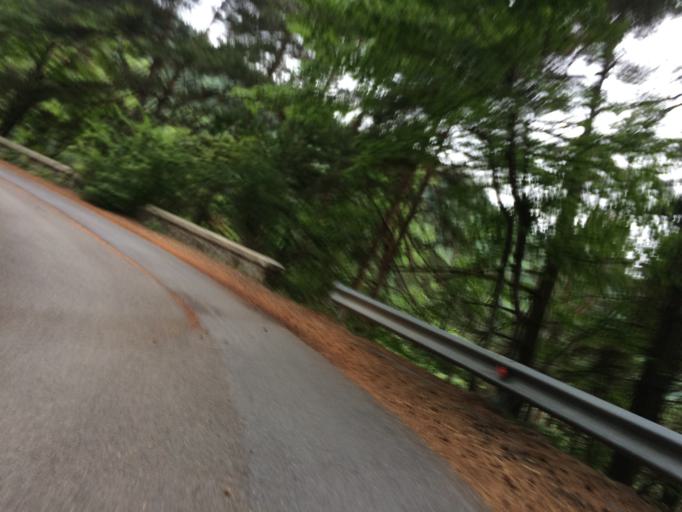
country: IT
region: Liguria
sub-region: Provincia di Imperia
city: Triora
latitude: 43.9677
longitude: 7.7426
